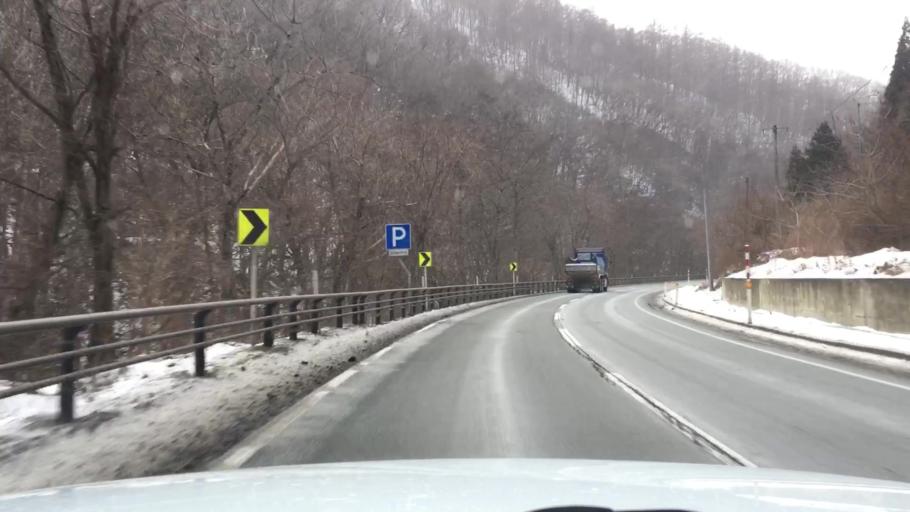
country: JP
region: Iwate
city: Tono
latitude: 39.6165
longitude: 141.5017
